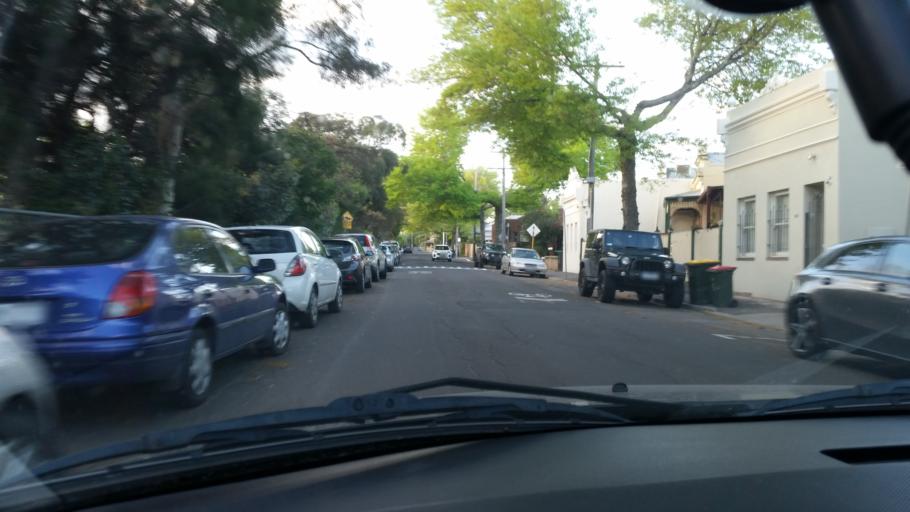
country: AU
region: Victoria
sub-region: Moonee Valley
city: Flemington
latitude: -37.7854
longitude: 144.9287
